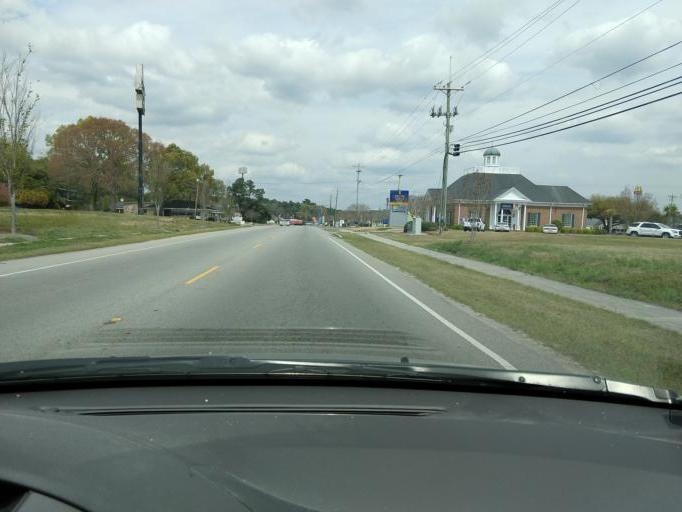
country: US
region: South Carolina
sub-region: Orangeburg County
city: Holly Hill
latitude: 33.4851
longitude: -80.4783
